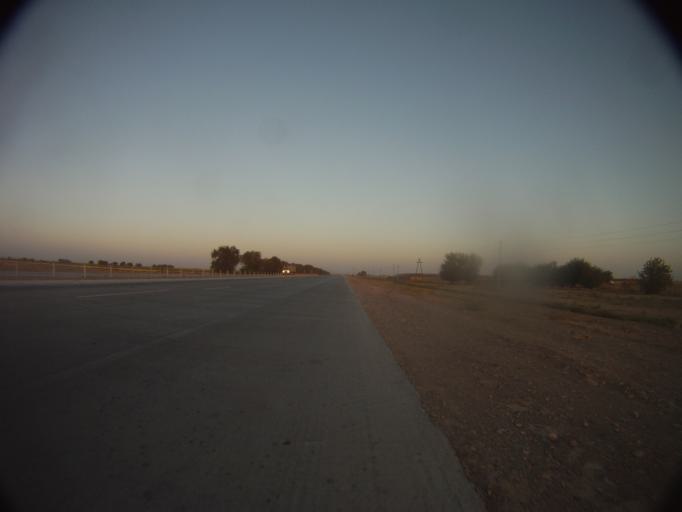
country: KZ
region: Ongtustik Qazaqstan
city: Turkestan
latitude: 43.2452
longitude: 68.4083
